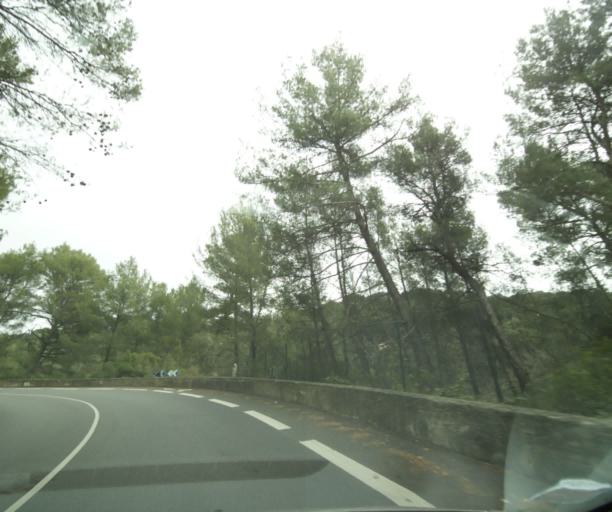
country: FR
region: Provence-Alpes-Cote d'Azur
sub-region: Departement des Bouches-du-Rhone
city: Aix-en-Provence
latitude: 43.5483
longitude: 5.4613
